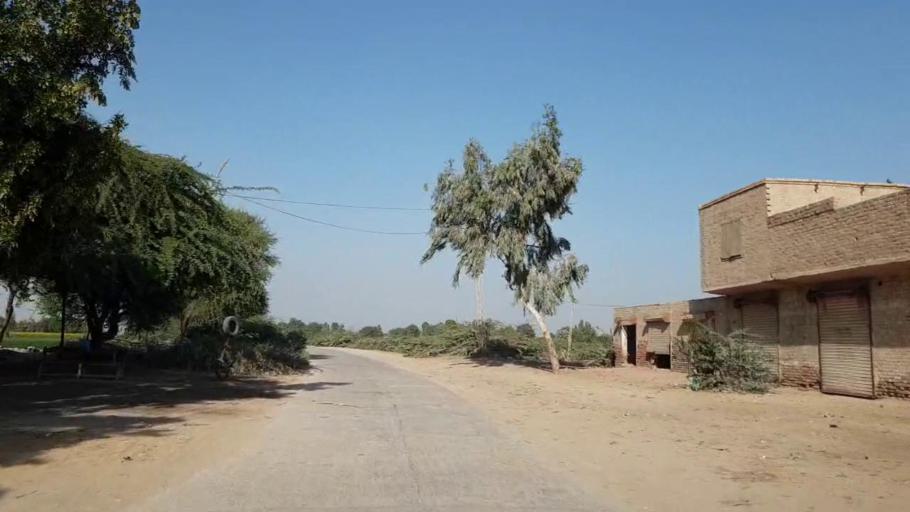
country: PK
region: Sindh
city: Digri
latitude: 25.1302
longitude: 69.1114
